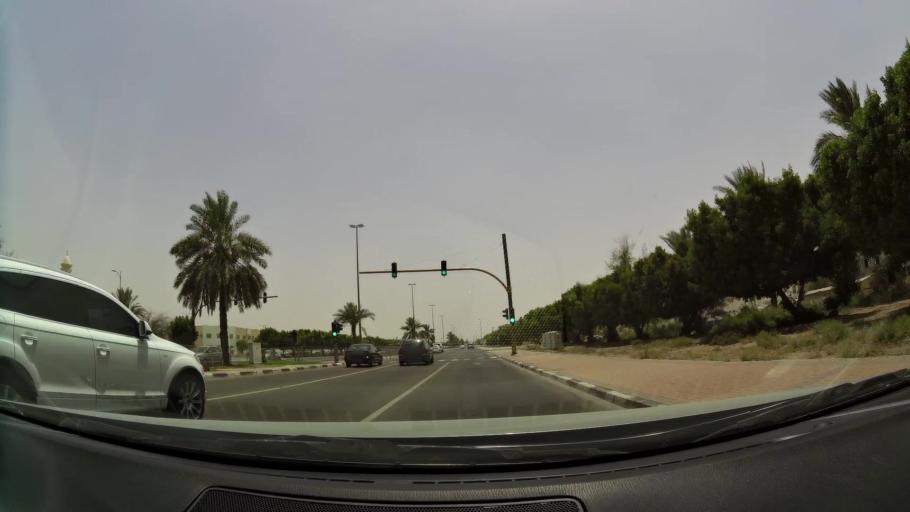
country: AE
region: Abu Dhabi
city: Al Ain
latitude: 24.2048
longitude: 55.7233
